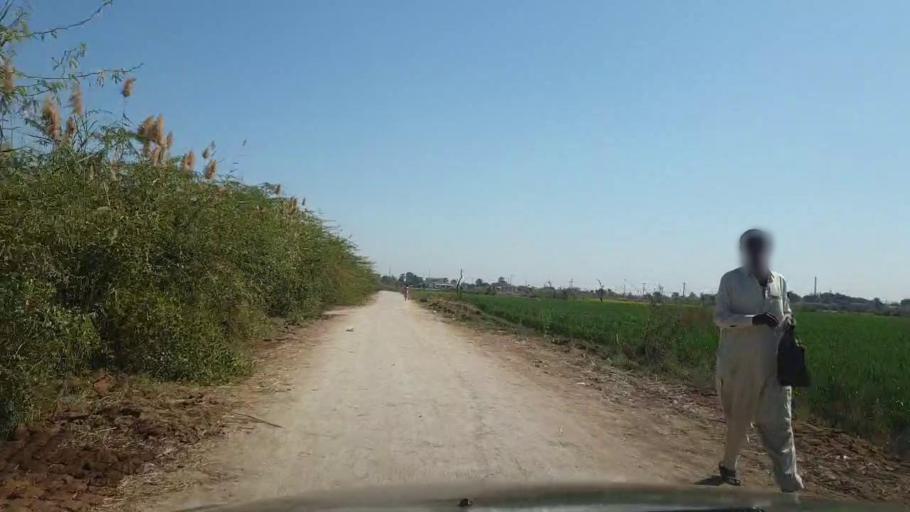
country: PK
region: Sindh
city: Mirpur Khas
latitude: 25.5696
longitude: 69.0614
